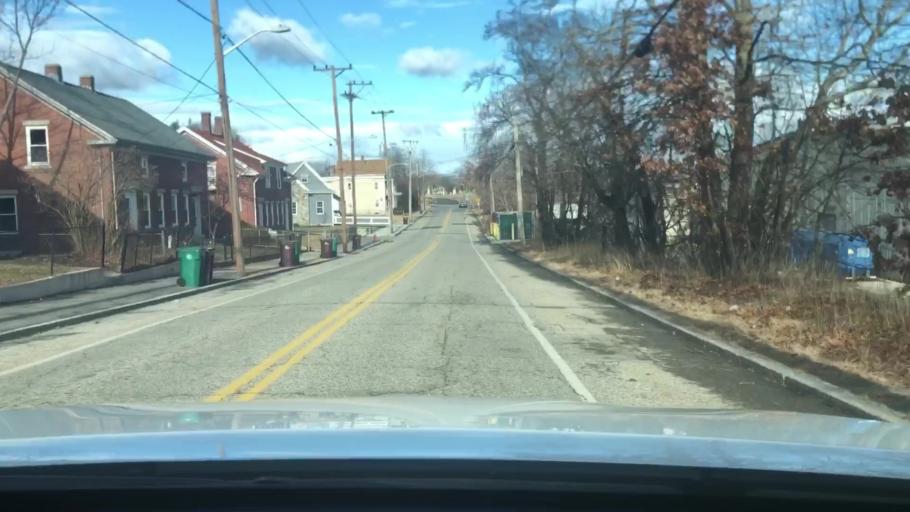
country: US
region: Rhode Island
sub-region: Providence County
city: Woonsocket
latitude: 42.0146
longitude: -71.5140
